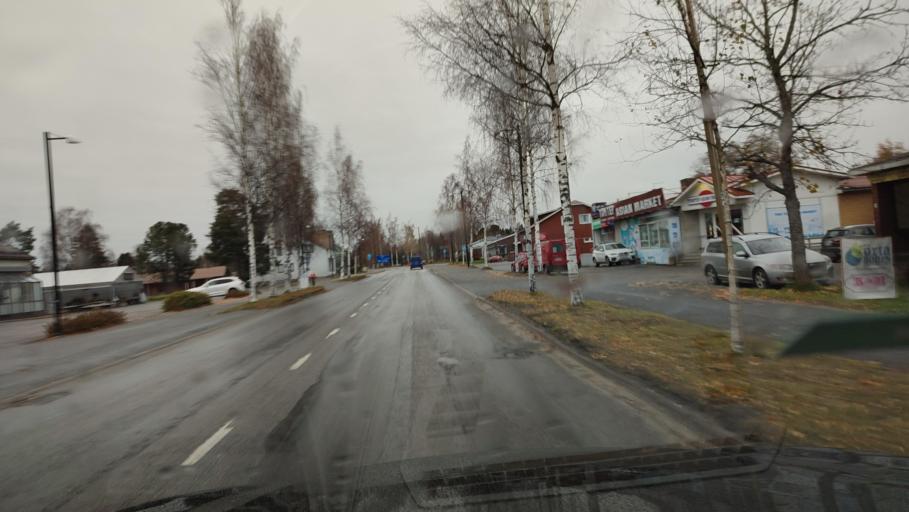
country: FI
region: Ostrobothnia
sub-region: Sydosterbotten
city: Naerpes
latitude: 62.4806
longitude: 21.3380
